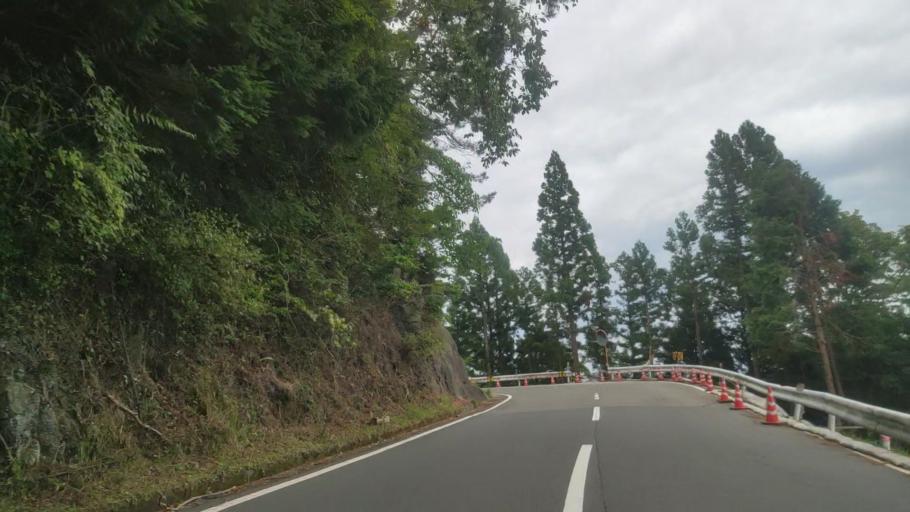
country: JP
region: Wakayama
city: Koya
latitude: 34.2171
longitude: 135.5682
